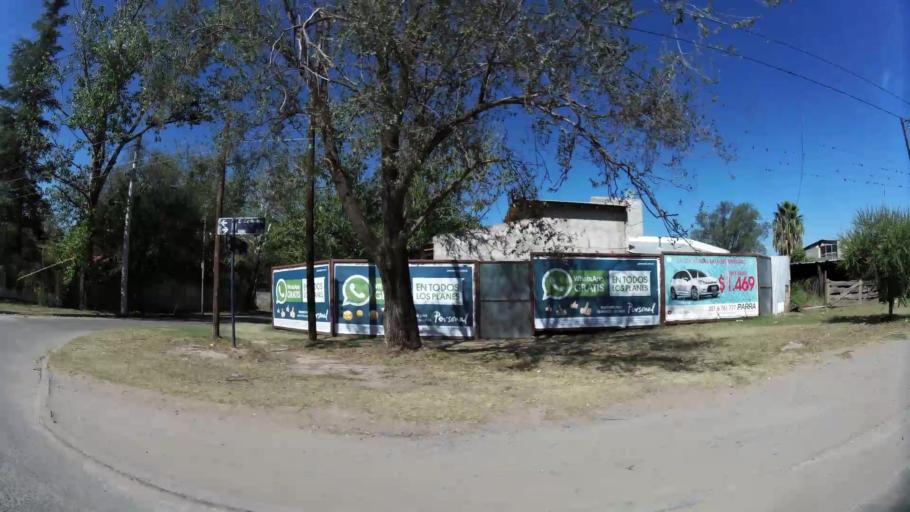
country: AR
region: Cordoba
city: Saldan
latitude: -31.3190
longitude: -64.2884
